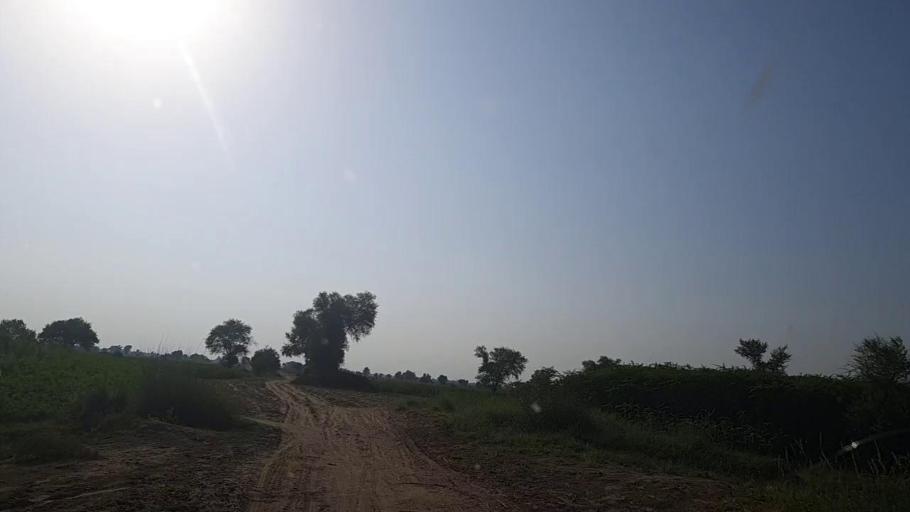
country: PK
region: Sindh
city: Khanpur
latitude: 27.7303
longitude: 69.3299
